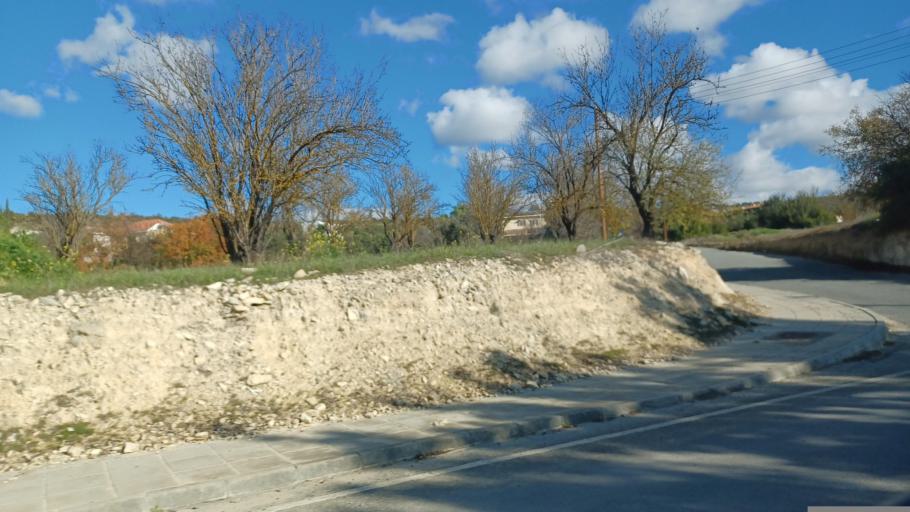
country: CY
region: Limassol
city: Pano Polemidia
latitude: 34.7632
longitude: 32.9986
